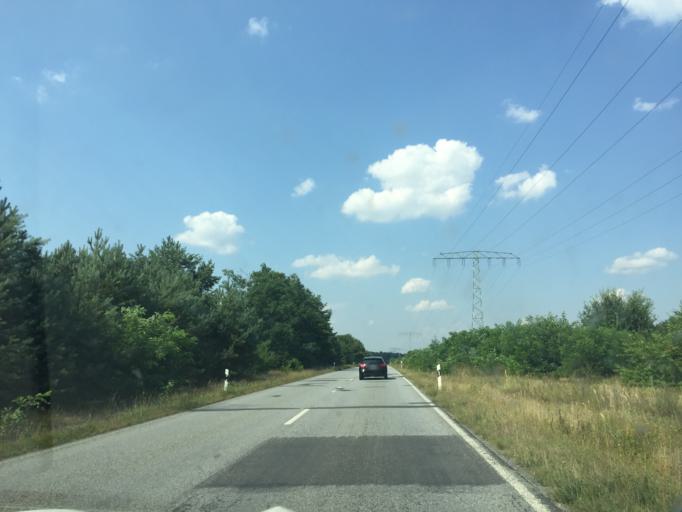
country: DE
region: Saxony
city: Boxberg
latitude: 51.4263
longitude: 14.5401
